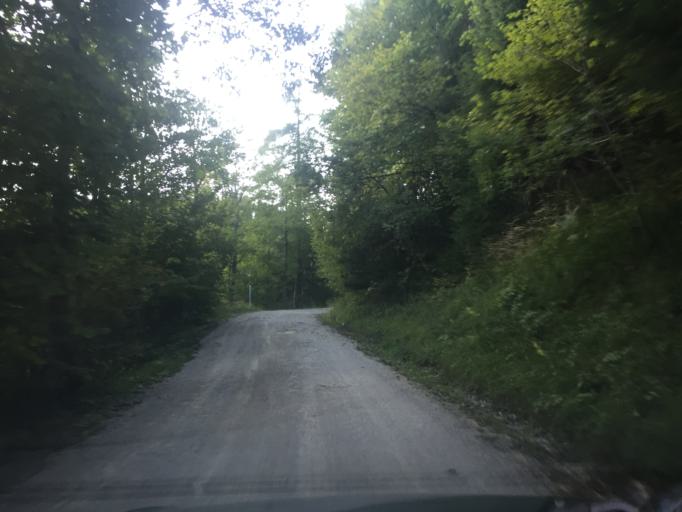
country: SI
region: Ravne na Koroskem
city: Kotlje
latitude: 46.4564
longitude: 14.9825
